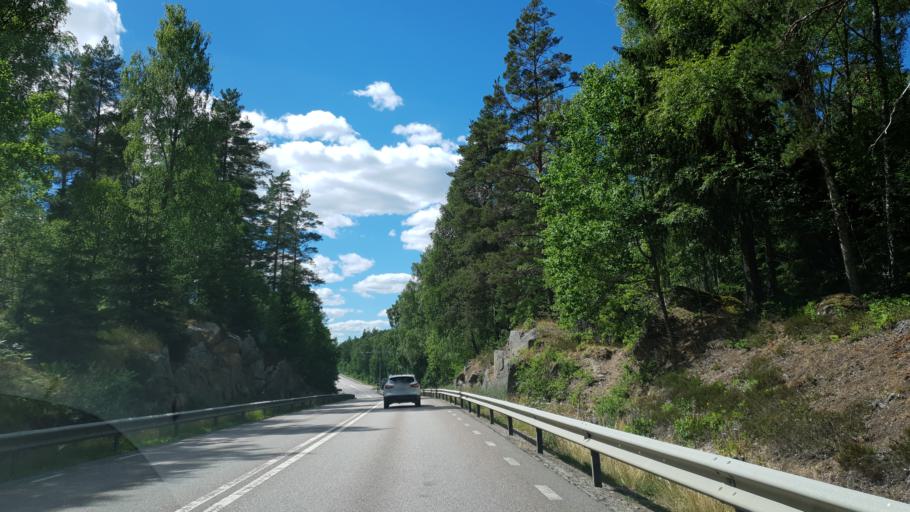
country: SE
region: Kronoberg
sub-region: Lessebo Kommun
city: Lessebo
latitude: 56.7821
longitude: 15.2272
